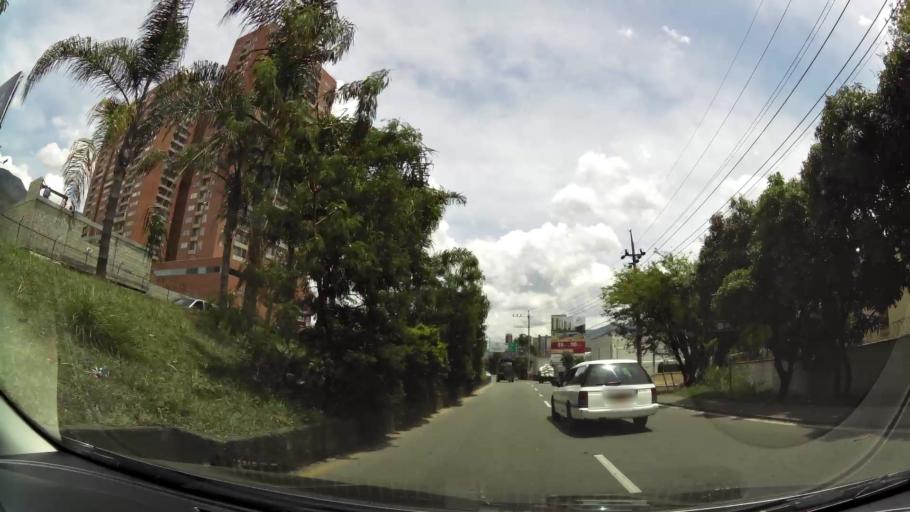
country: CO
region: Antioquia
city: Bello
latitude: 6.3359
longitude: -75.5505
